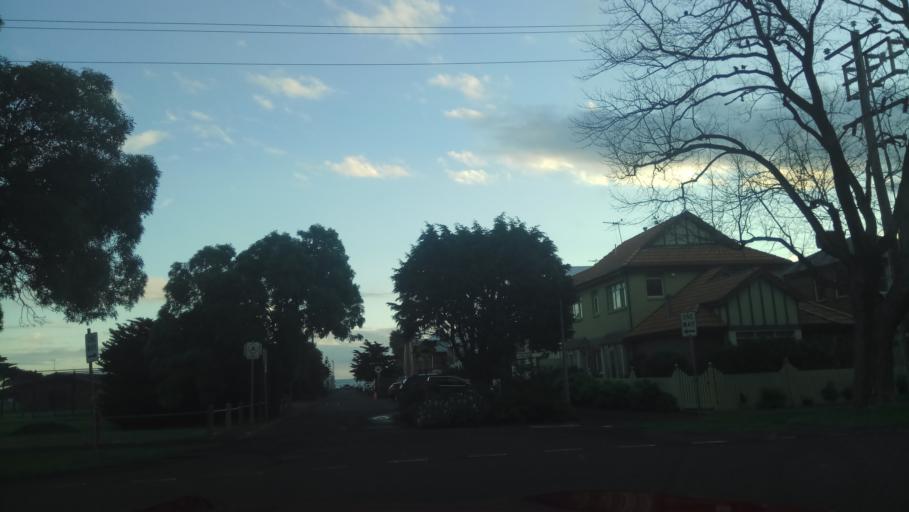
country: AU
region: Victoria
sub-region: Hobsons Bay
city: Williamstown
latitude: -37.8654
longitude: 144.8947
